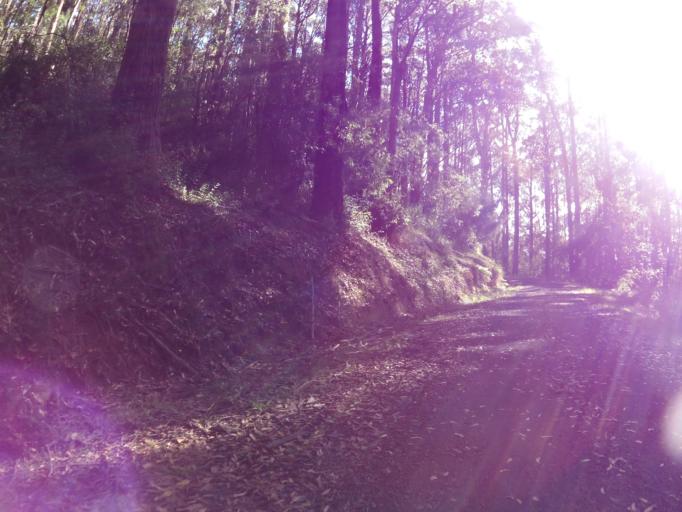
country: AU
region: Victoria
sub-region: Yarra Ranges
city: Millgrove
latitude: -37.8496
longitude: 145.7986
